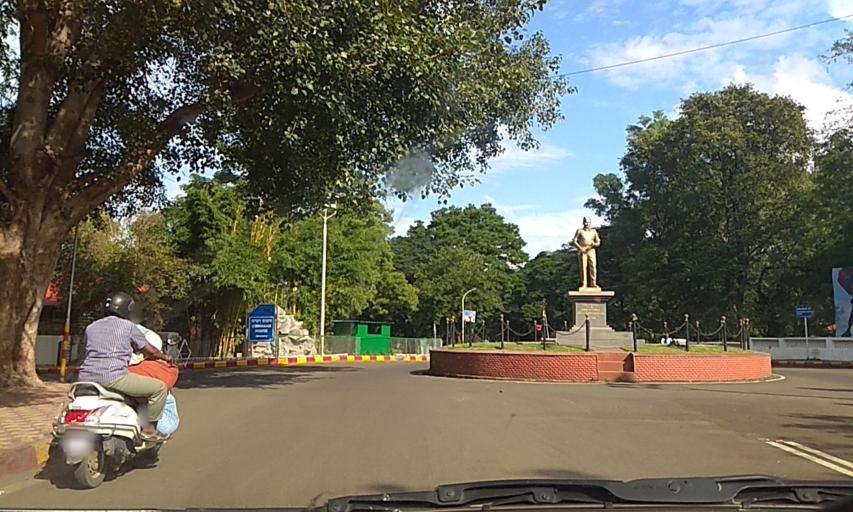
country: IN
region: Maharashtra
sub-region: Pune Division
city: Pune
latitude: 18.5238
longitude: 73.8827
